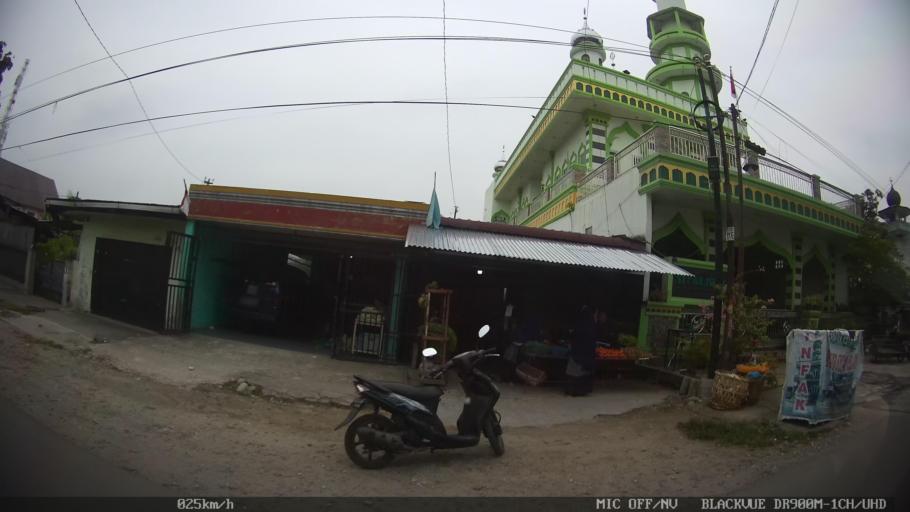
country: ID
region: North Sumatra
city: Medan
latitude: 3.5529
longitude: 98.7013
